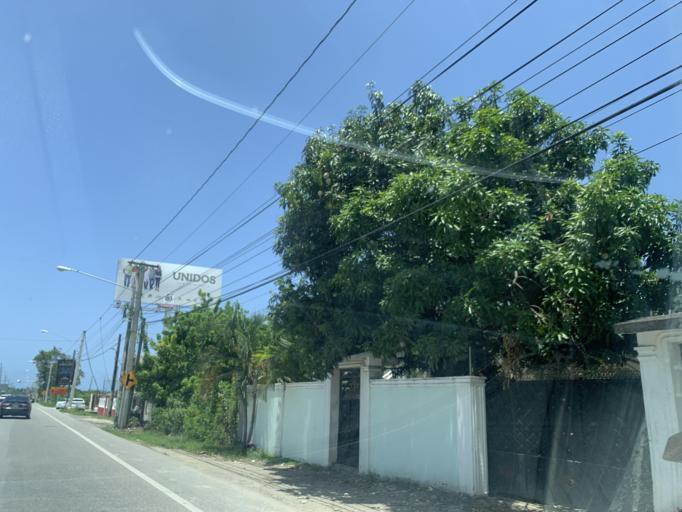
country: DO
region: Puerto Plata
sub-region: Puerto Plata
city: Puerto Plata
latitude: 19.7380
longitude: -70.6029
